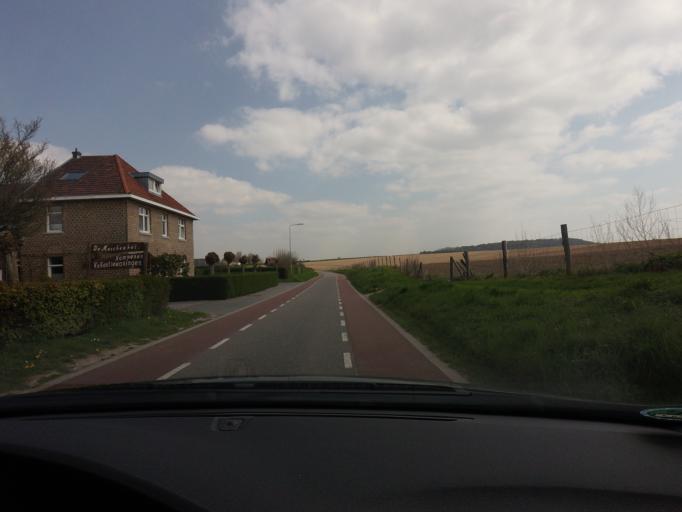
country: NL
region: Limburg
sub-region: Eijsden-Margraten
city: Eijsden
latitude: 50.7746
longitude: 5.7505
